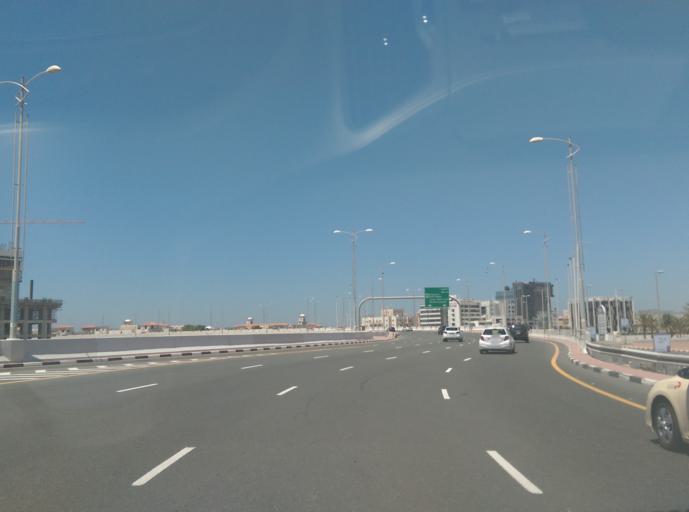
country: AE
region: Dubai
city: Dubai
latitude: 25.0975
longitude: 55.1621
